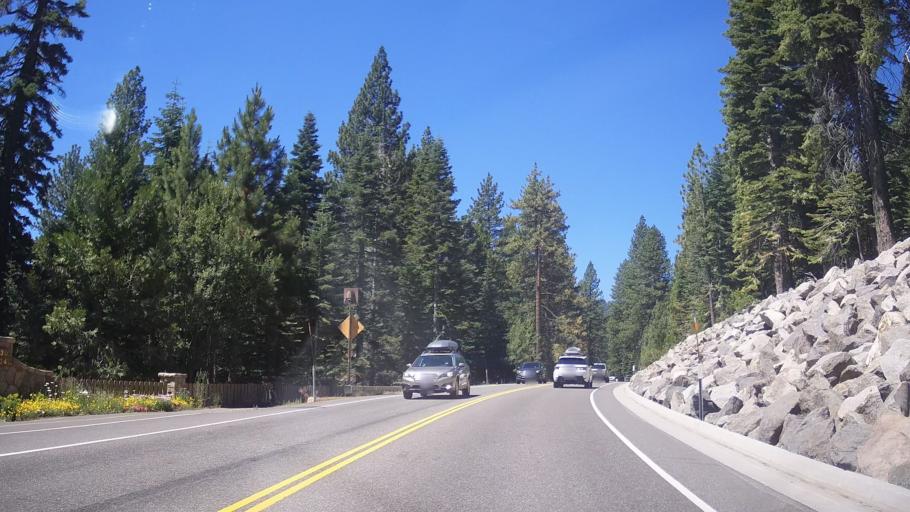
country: US
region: California
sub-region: Placer County
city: Sunnyside-Tahoe City
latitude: 39.1470
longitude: -120.1483
